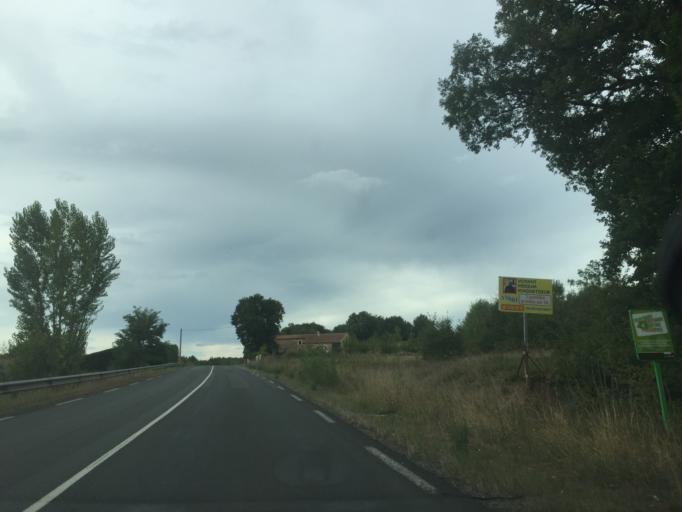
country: FR
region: Aquitaine
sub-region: Departement du Lot-et-Garonne
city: Monsempron-Libos
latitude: 44.5017
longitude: 0.9476
